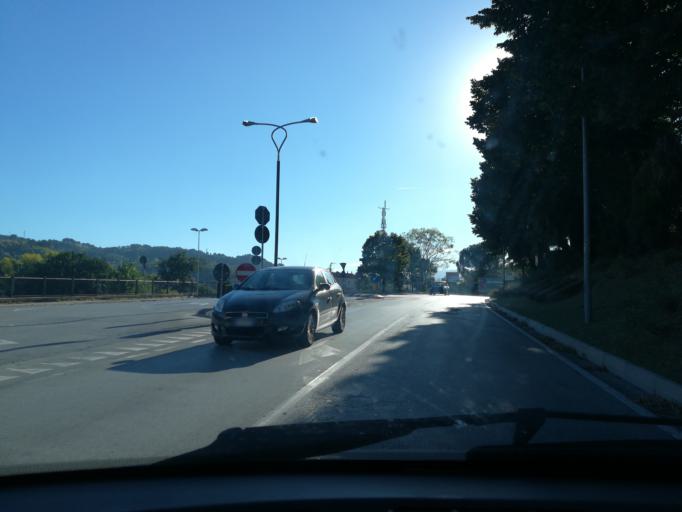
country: IT
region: The Marches
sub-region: Provincia di Macerata
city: Tolentino
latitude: 43.2107
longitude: 13.2959
